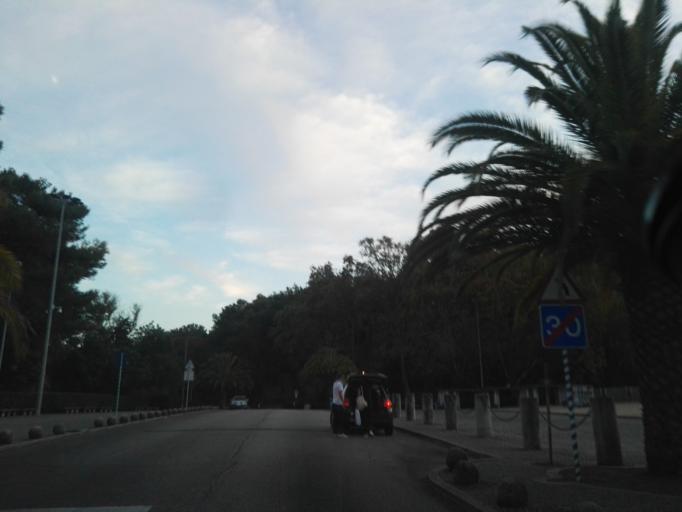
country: PT
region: Lisbon
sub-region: Oeiras
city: Quejas
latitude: 38.7092
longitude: -9.2588
